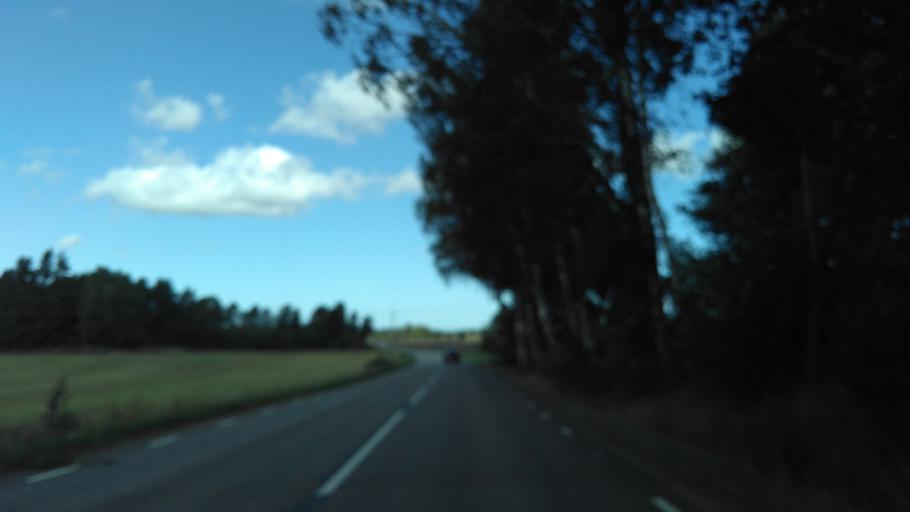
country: SE
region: Vaestra Goetaland
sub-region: Vara Kommun
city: Vara
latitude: 58.1834
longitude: 13.0017
